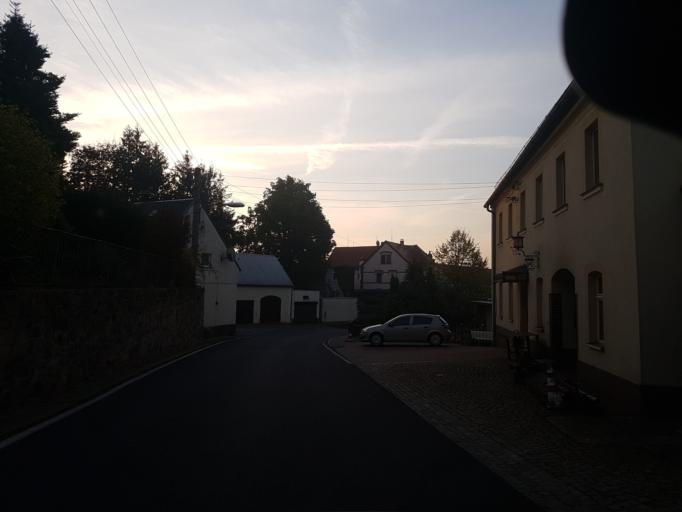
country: DE
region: Saxony
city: Grossweitzschen
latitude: 51.1322
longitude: 13.0612
